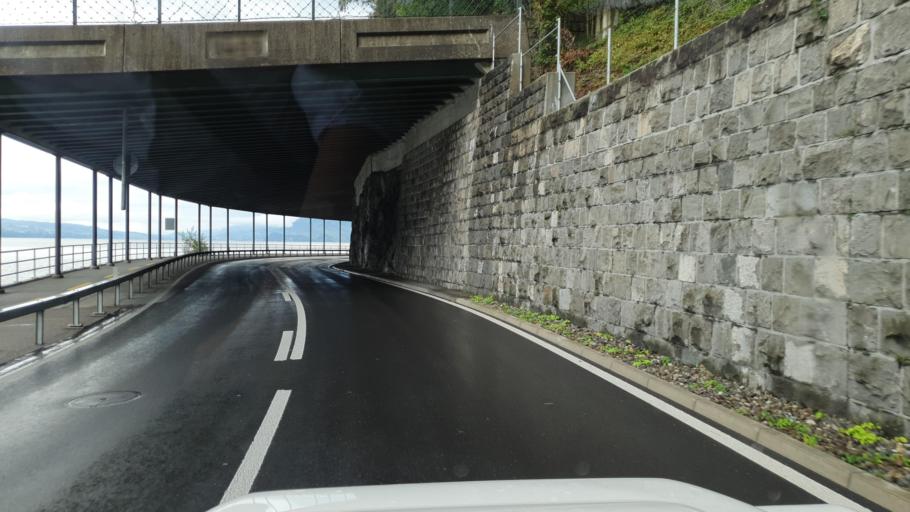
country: CH
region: Nidwalden
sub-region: Nidwalden
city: Stansstad
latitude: 46.9792
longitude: 8.3259
